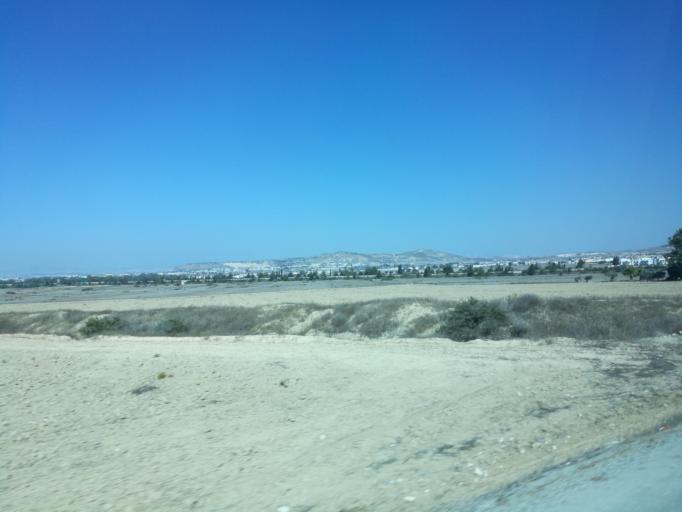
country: CY
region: Larnaka
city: Pyla
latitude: 34.9882
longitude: 33.6978
